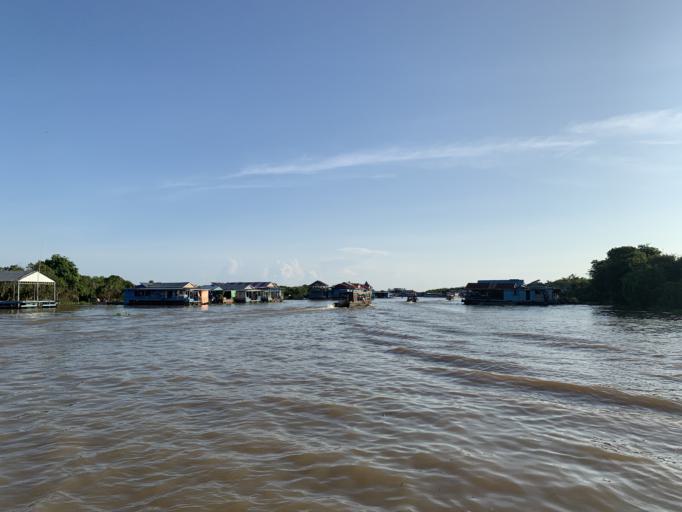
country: KH
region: Siem Reap
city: Siem Reap
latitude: 13.2462
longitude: 103.8232
